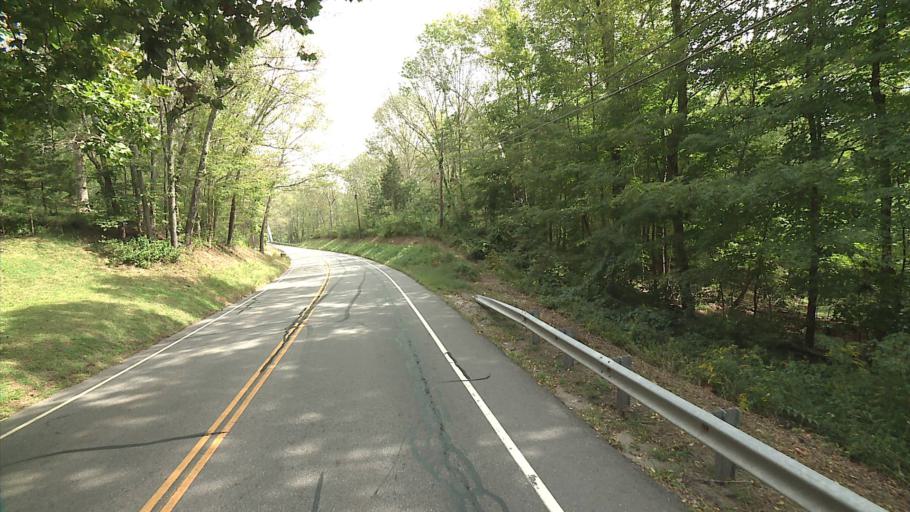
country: US
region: Connecticut
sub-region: New London County
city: Jewett City
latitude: 41.6513
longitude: -71.9732
